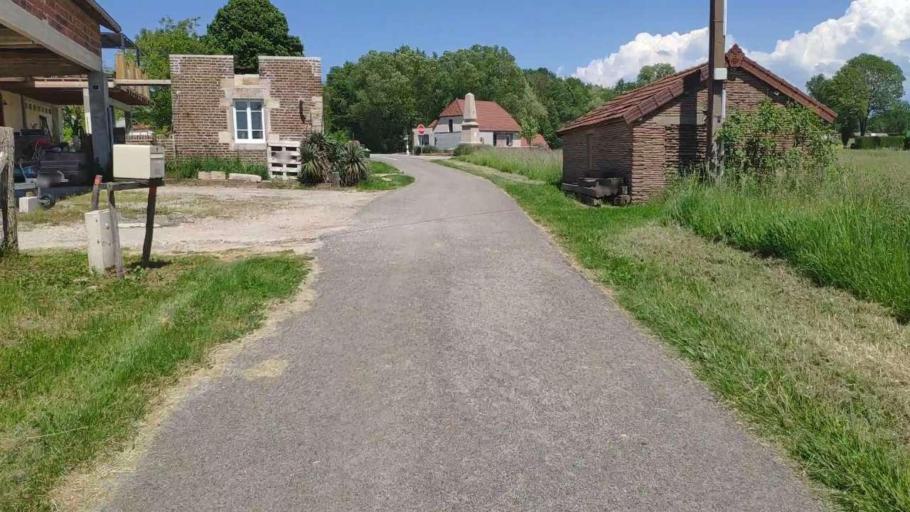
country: FR
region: Franche-Comte
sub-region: Departement du Jura
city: Bletterans
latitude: 46.7442
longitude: 5.4006
